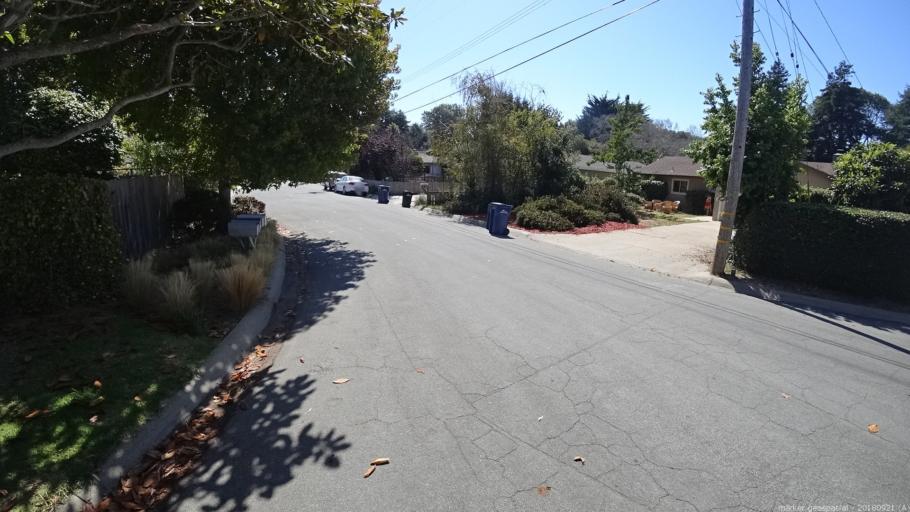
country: US
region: California
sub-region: Monterey County
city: Carmel-by-the-Sea
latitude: 36.5407
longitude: -121.9172
